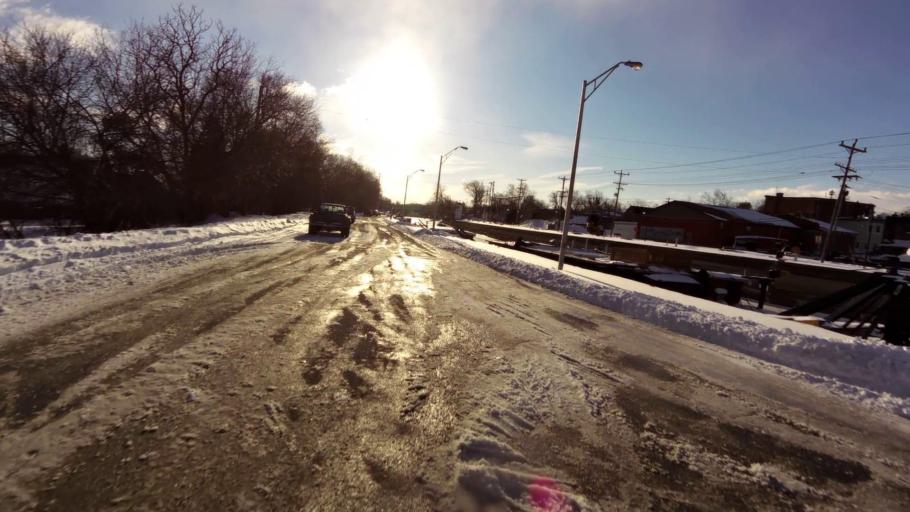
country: US
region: New York
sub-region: Orleans County
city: Albion
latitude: 43.2493
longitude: -78.1931
